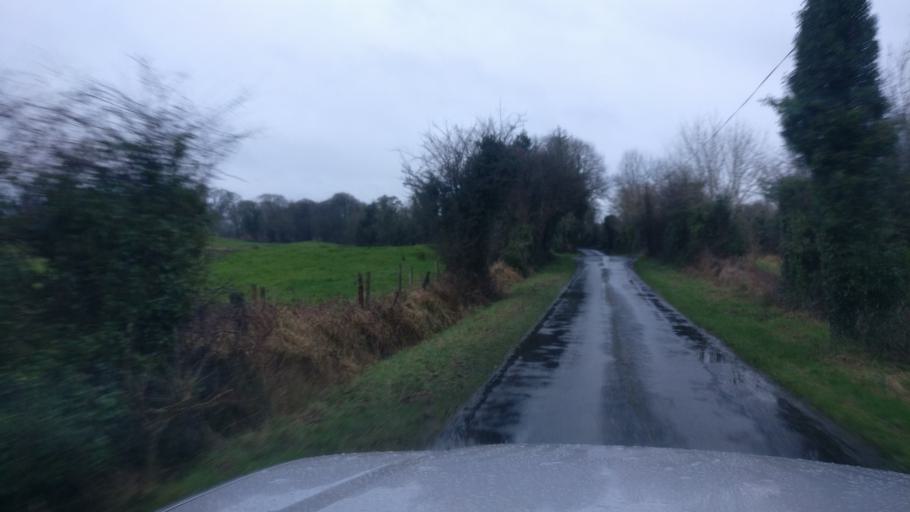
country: IE
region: Connaught
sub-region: County Galway
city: Ballinasloe
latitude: 53.2825
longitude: -8.3014
